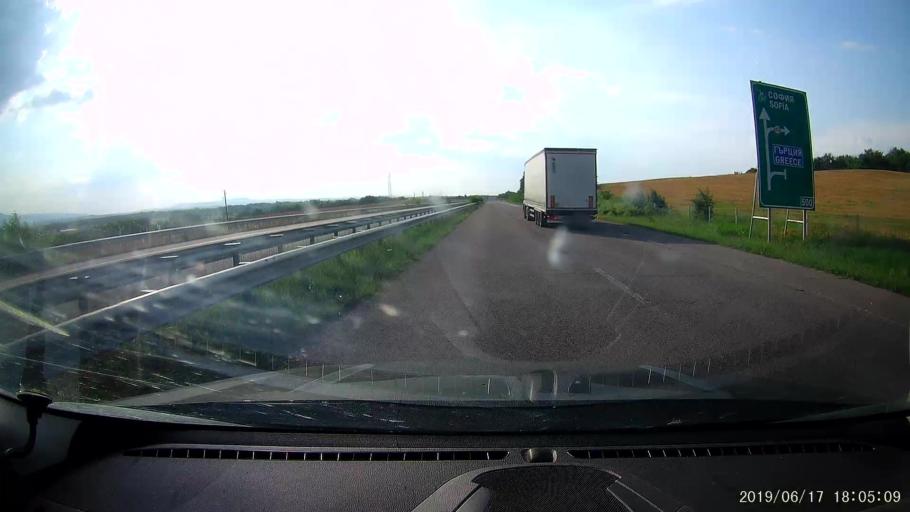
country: BG
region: Khaskovo
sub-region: Obshtina Svilengrad
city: Svilengrad
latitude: 41.7946
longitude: 26.1822
